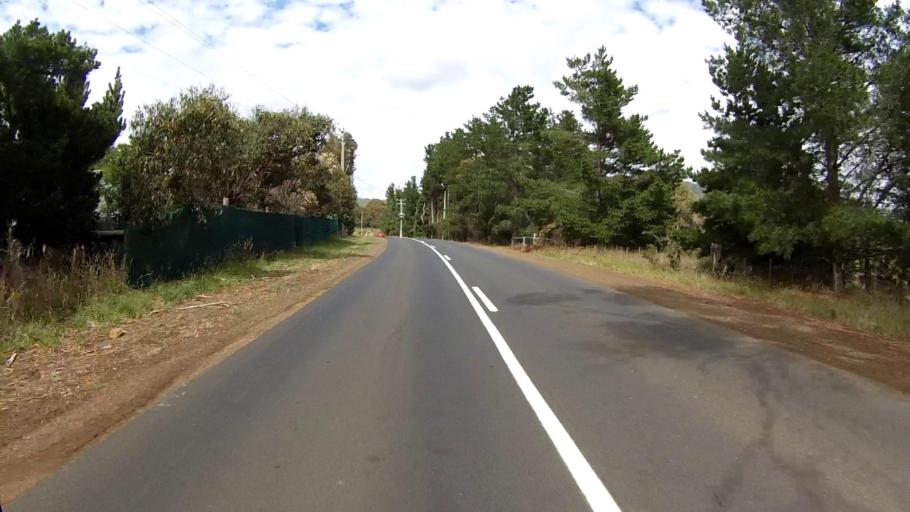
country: AU
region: Tasmania
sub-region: Clarence
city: Cambridge
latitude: -42.7623
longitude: 147.3963
